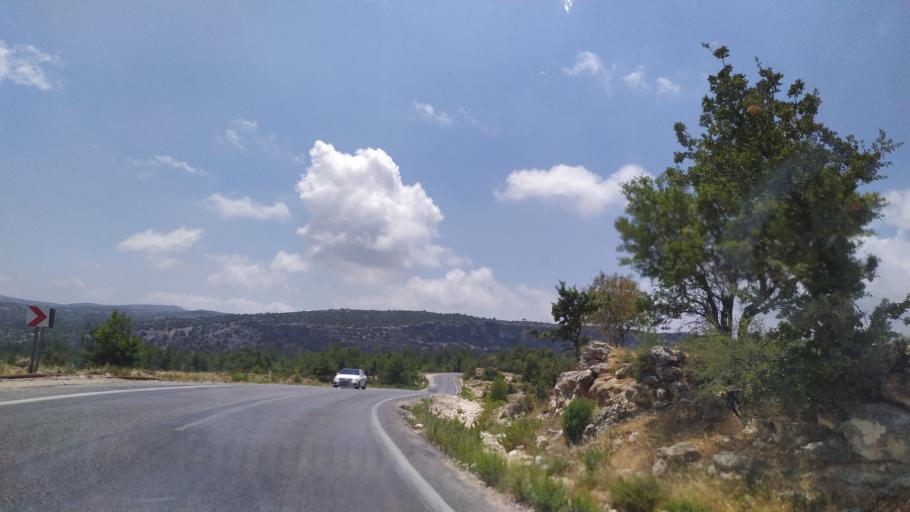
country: TR
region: Mersin
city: Gulnar
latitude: 36.2802
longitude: 33.3891
